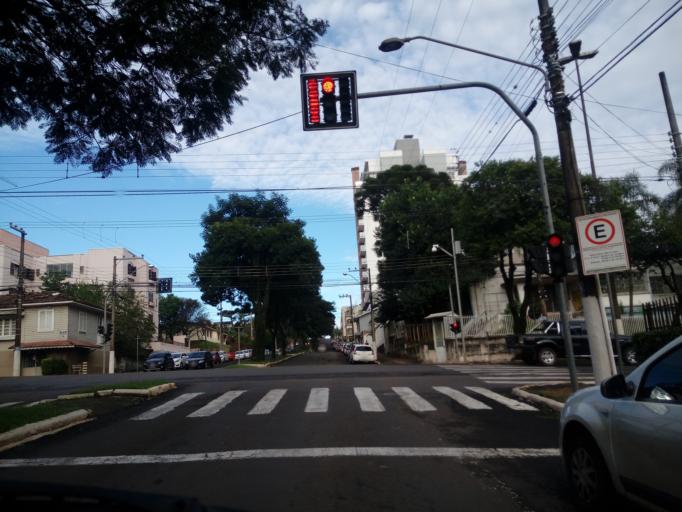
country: BR
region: Santa Catarina
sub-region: Chapeco
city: Chapeco
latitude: -27.1057
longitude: -52.6189
